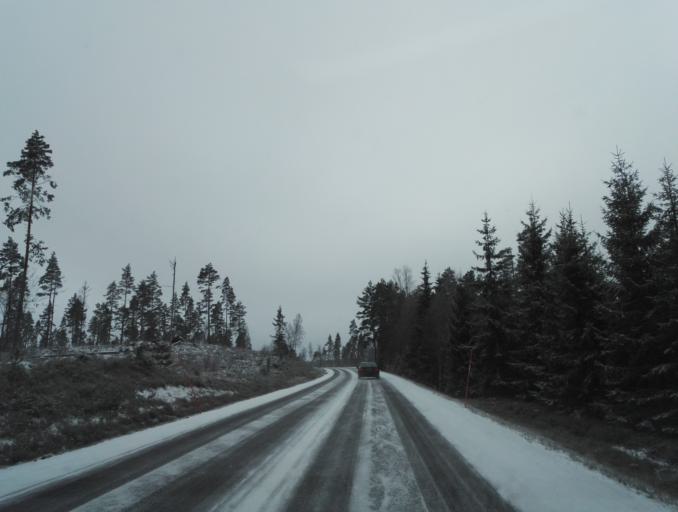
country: SE
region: Kronoberg
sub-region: Lessebo Kommun
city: Lessebo
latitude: 56.7821
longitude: 15.3055
